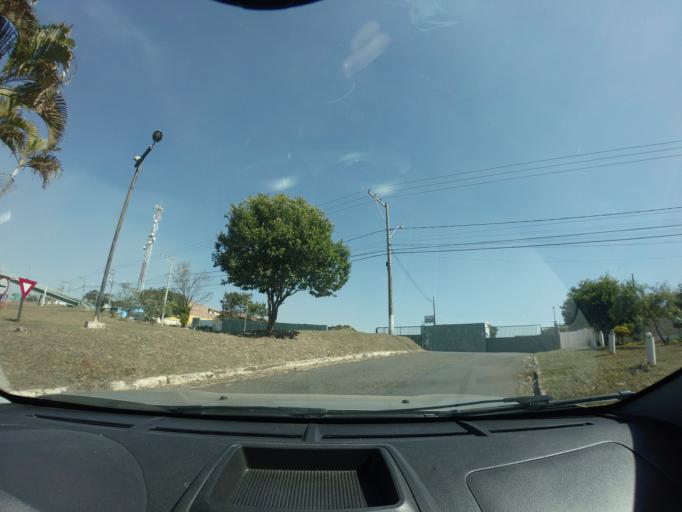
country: BR
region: Sao Paulo
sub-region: Piracicaba
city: Piracicaba
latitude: -22.7555
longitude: -47.5977
